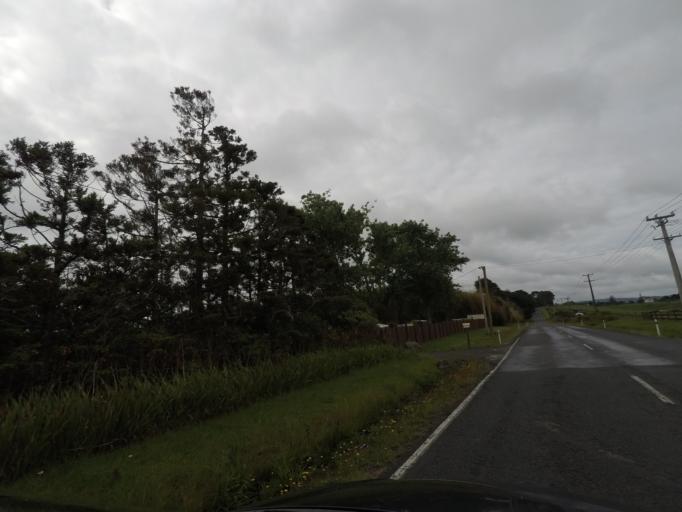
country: NZ
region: Auckland
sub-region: Auckland
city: Rosebank
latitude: -36.8262
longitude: 174.5763
